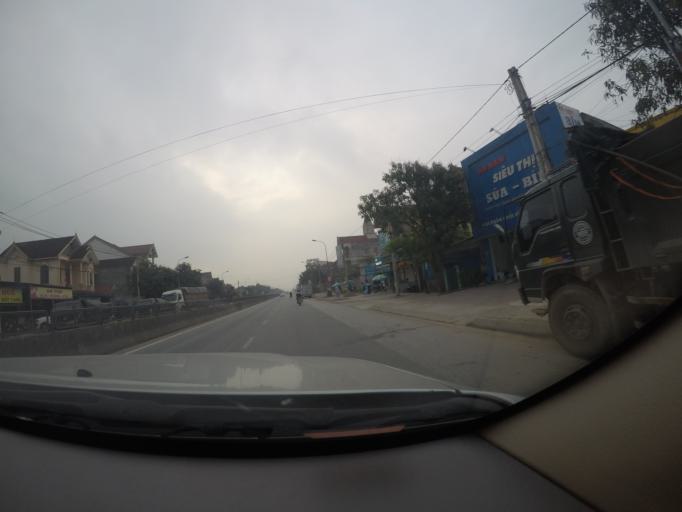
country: VN
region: Ha Tinh
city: Cam Xuyen
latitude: 18.2489
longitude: 106.0025
